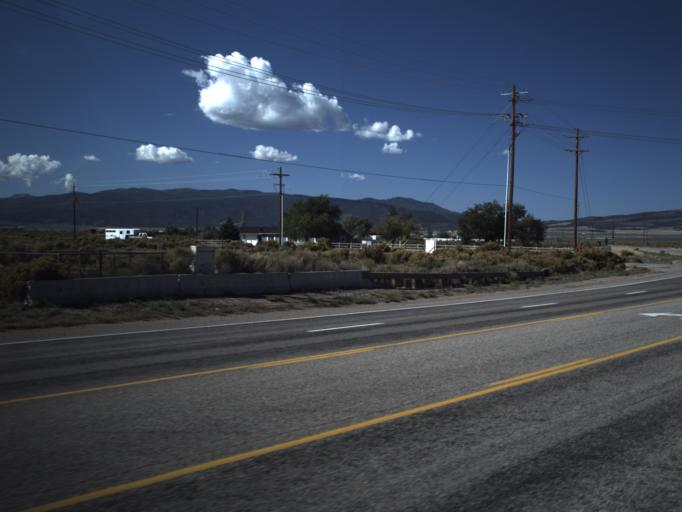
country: US
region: Utah
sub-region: Iron County
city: Cedar City
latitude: 37.6850
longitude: -113.1603
